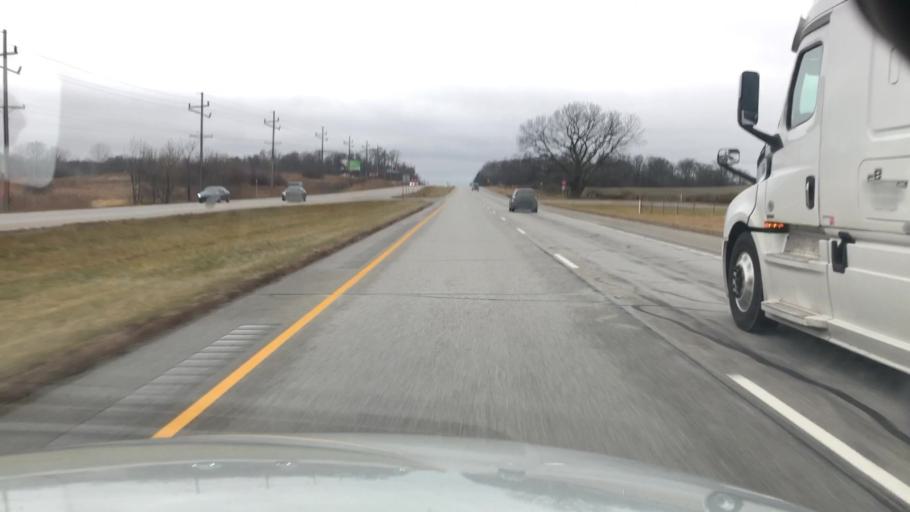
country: US
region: Indiana
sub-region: Kosciusko County
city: Pierceton
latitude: 41.2065
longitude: -85.7134
